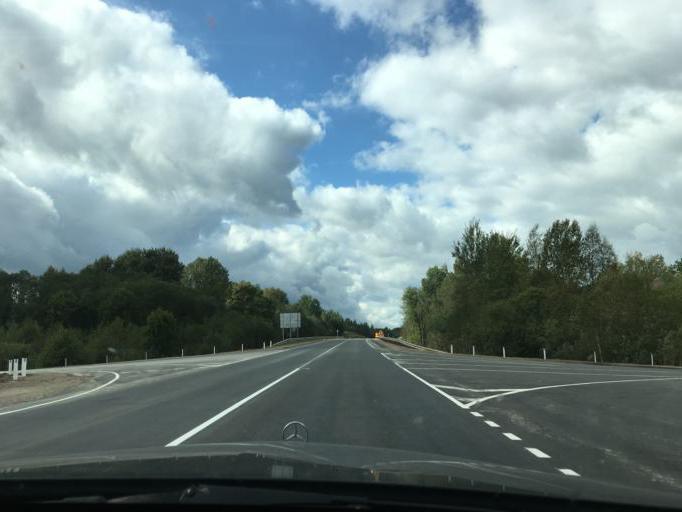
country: RU
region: Tverskaya
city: Toropets
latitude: 56.3134
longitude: 31.1561
